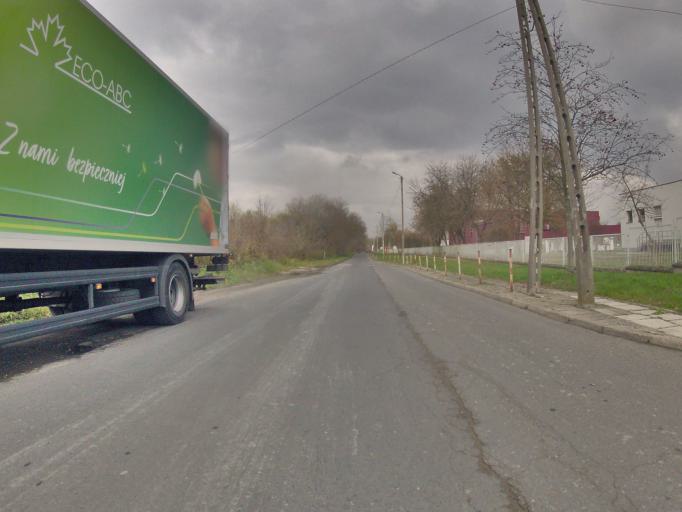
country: PL
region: Lesser Poland Voivodeship
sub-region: Powiat wielicki
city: Wegrzce Wielkie
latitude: 50.0529
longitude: 20.1018
